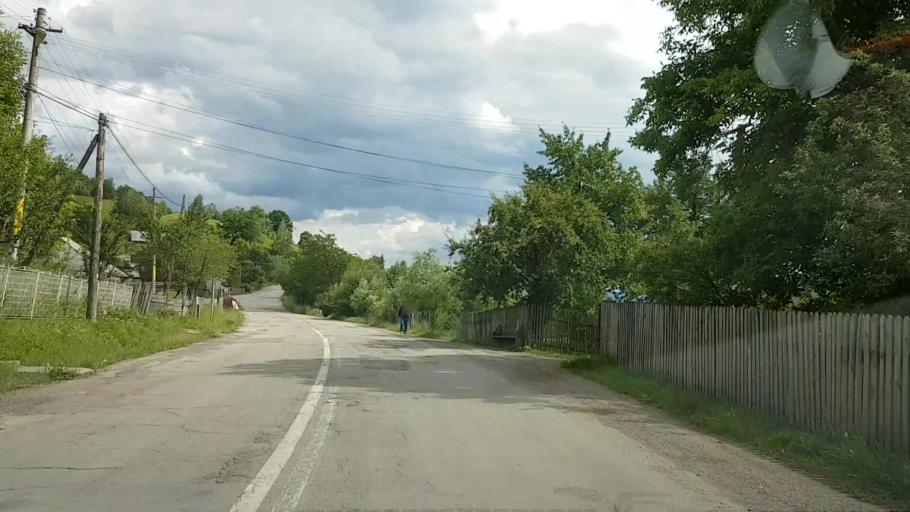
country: RO
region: Neamt
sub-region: Comuna Hangu
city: Hangu
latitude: 47.0434
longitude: 26.0545
